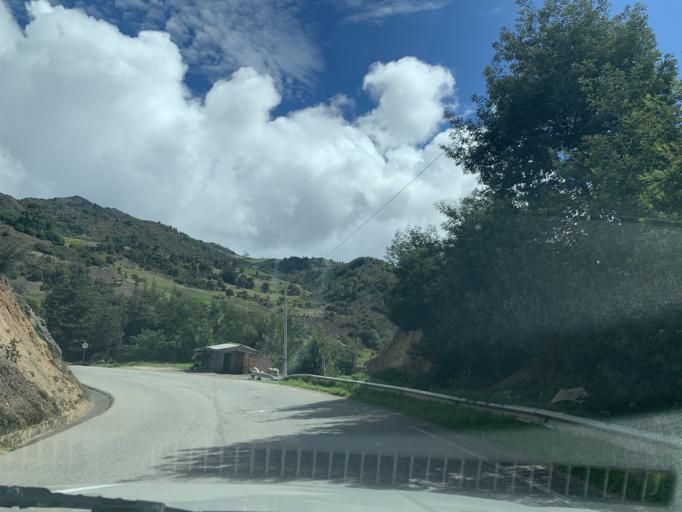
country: CO
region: Boyaca
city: Aquitania
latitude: 5.6138
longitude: -72.8784
